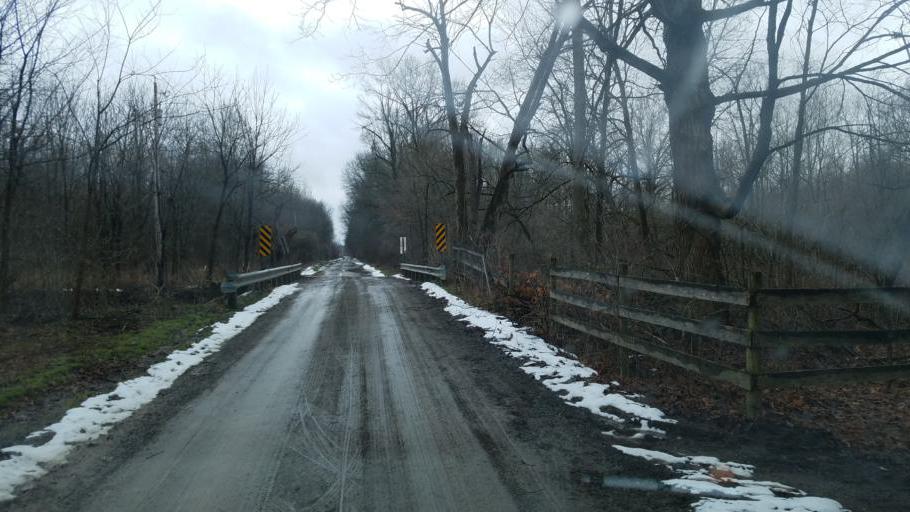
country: US
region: Ohio
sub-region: Ashtabula County
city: Orwell
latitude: 41.4360
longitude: -80.9350
